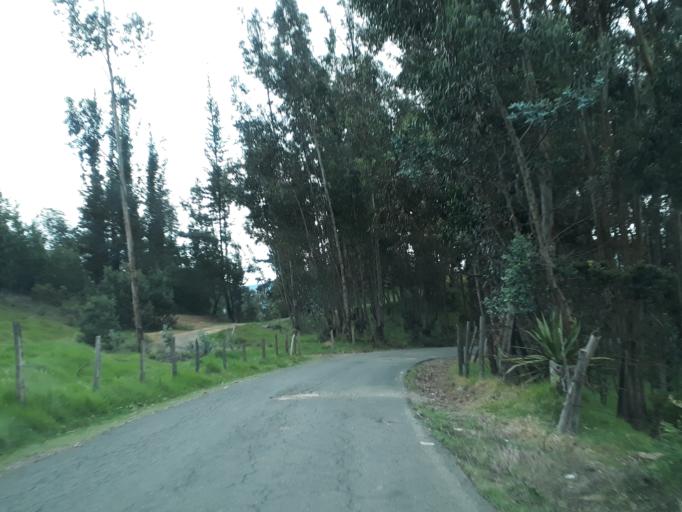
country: CO
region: Cundinamarca
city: Susa
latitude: 5.4029
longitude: -73.7692
